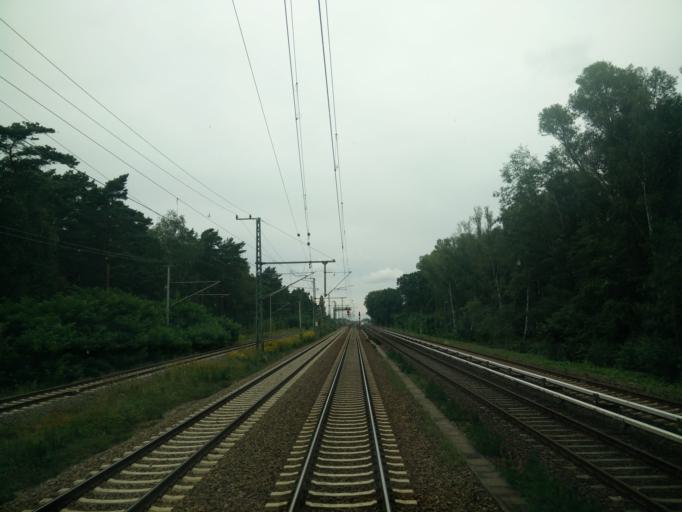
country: DE
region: Berlin
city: Grunau
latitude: 52.4009
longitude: 13.5912
